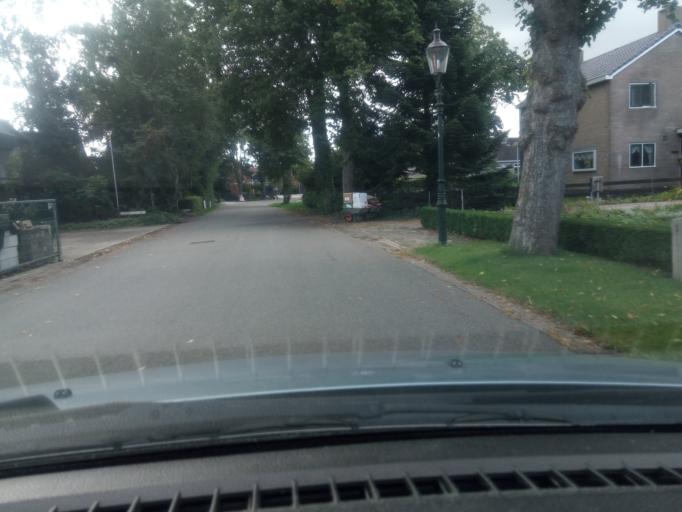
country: NL
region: Groningen
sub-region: Gemeente Zuidhorn
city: Grijpskerk
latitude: 53.2653
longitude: 6.2513
